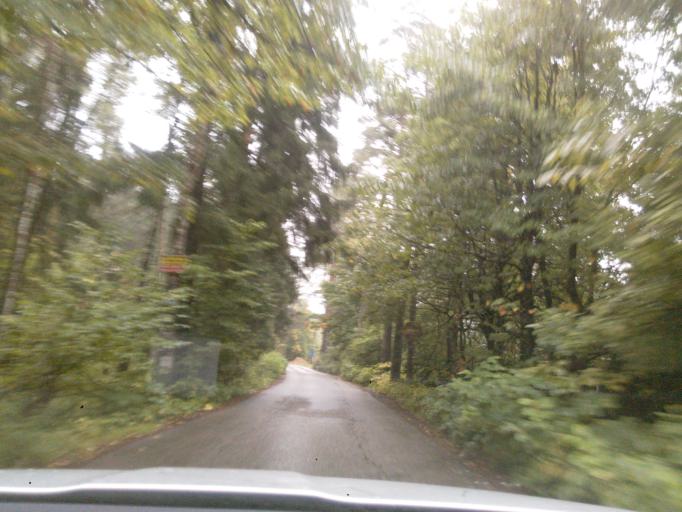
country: RU
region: Moskovskaya
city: Lozhki
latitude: 56.0451
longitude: 37.1055
